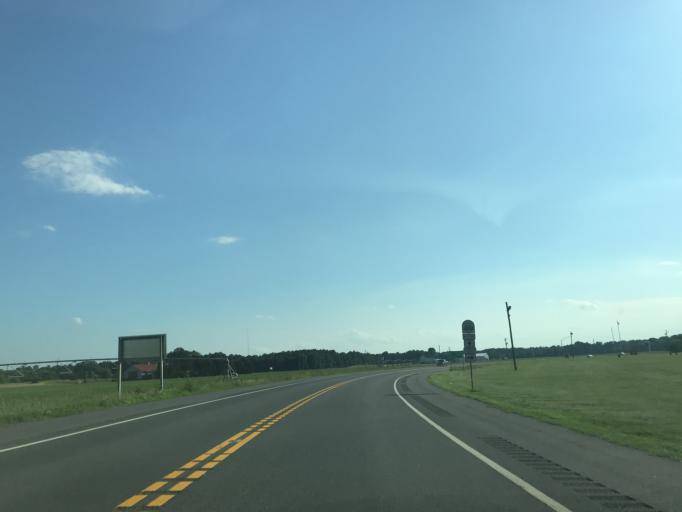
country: US
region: Maryland
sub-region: Wicomico County
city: Hebron
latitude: 38.5347
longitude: -75.7122
